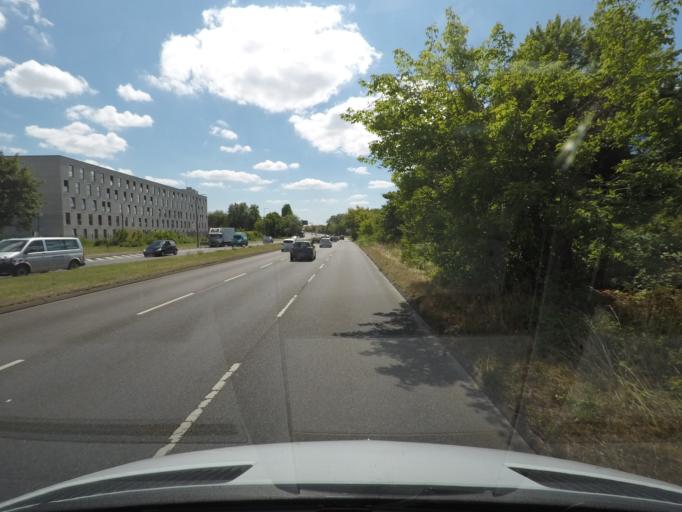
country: DE
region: Berlin
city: Falkenberg
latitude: 52.5390
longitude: 13.5388
